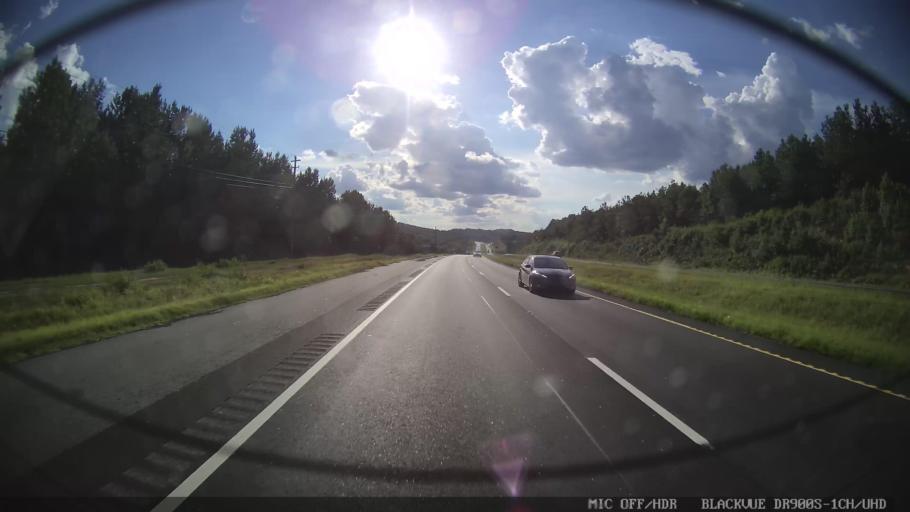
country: US
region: Georgia
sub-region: Floyd County
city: Rome
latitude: 34.2152
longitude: -85.1191
